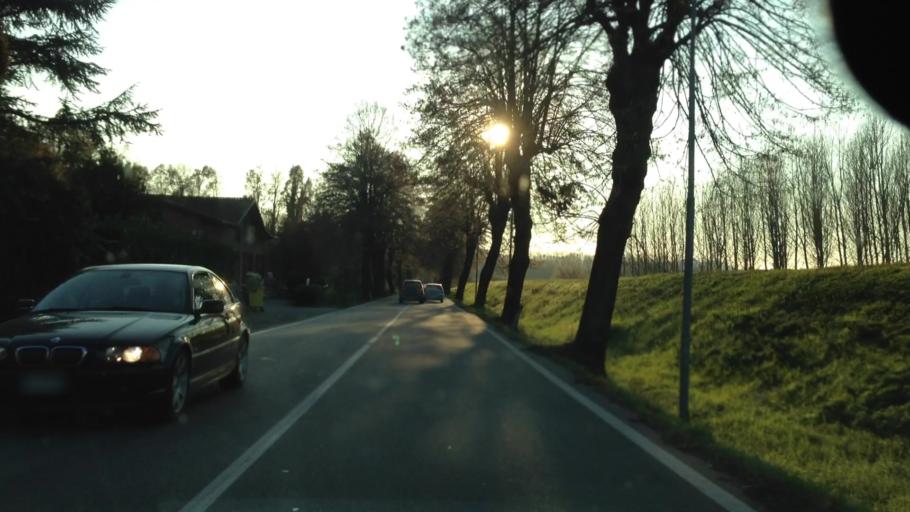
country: IT
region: Piedmont
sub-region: Provincia di Torino
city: Verrua Savoia
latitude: 45.1719
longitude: 8.0944
